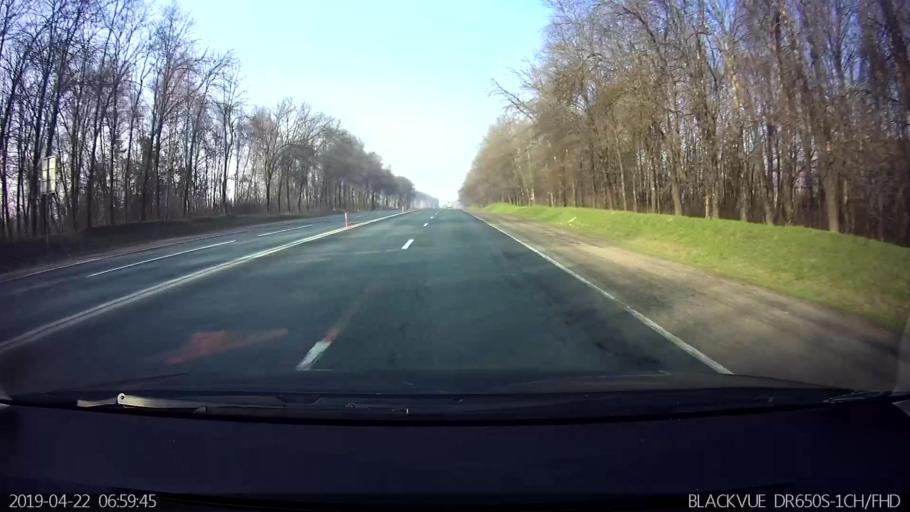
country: RU
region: Smolensk
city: Gagarin
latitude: 55.4248
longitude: 34.7996
